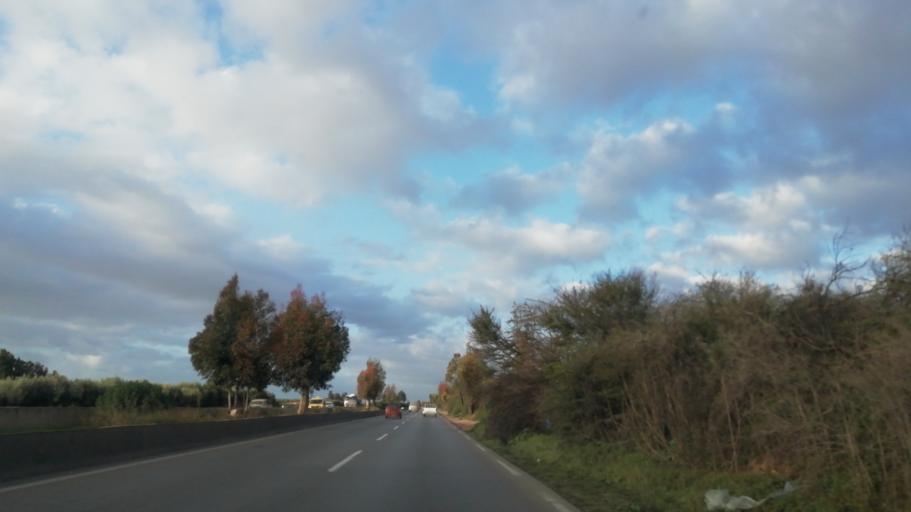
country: DZ
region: Oran
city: Bou Tlelis
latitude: 35.5996
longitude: -0.7738
